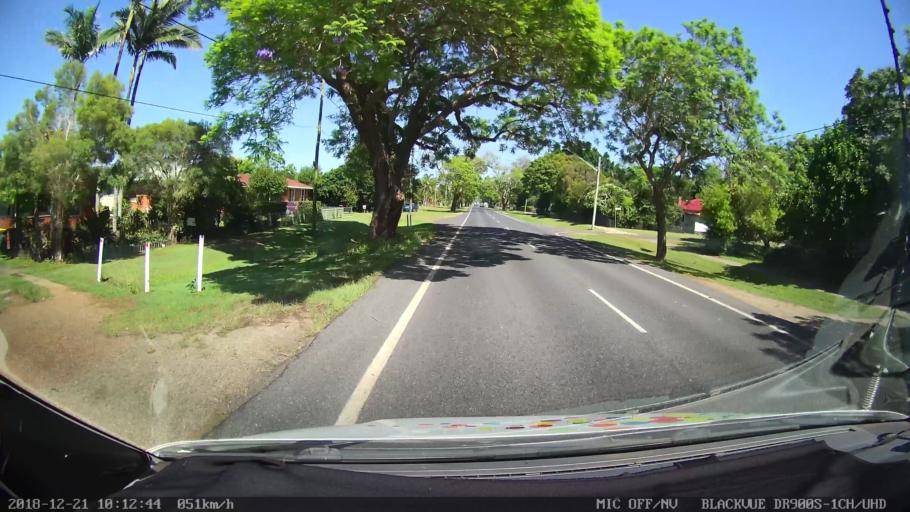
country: AU
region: New South Wales
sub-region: Clarence Valley
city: South Grafton
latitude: -29.6993
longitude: 152.9218
